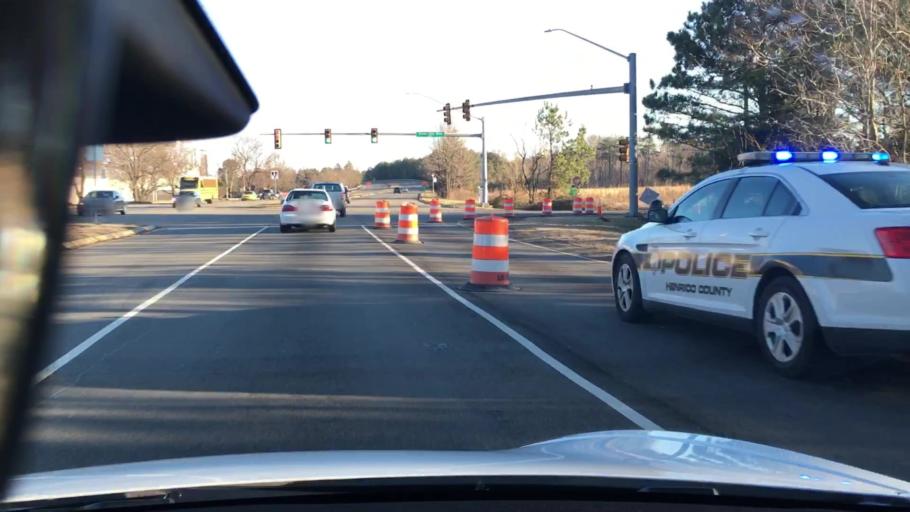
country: US
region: Virginia
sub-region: Henrico County
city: Fort Lee
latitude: 37.4927
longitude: -77.3530
